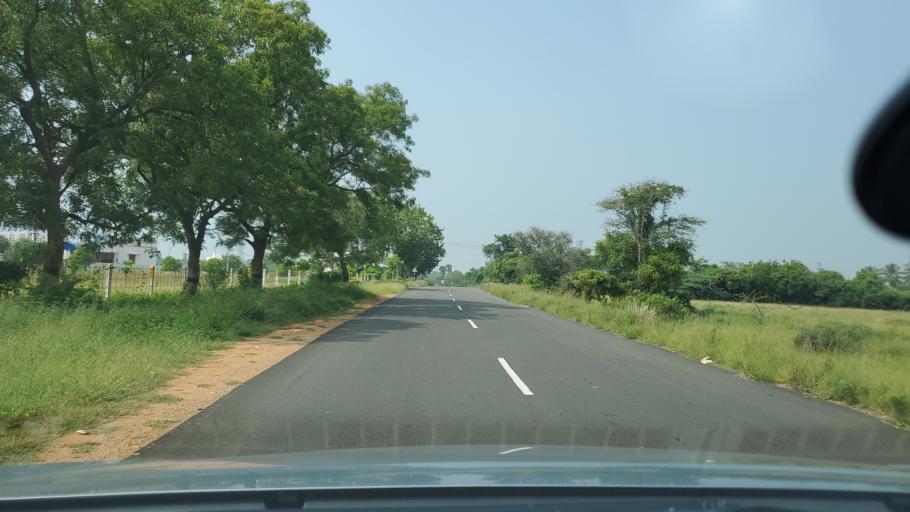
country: IN
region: Tamil Nadu
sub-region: Erode
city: Chennimalai
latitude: 11.2001
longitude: 77.6309
